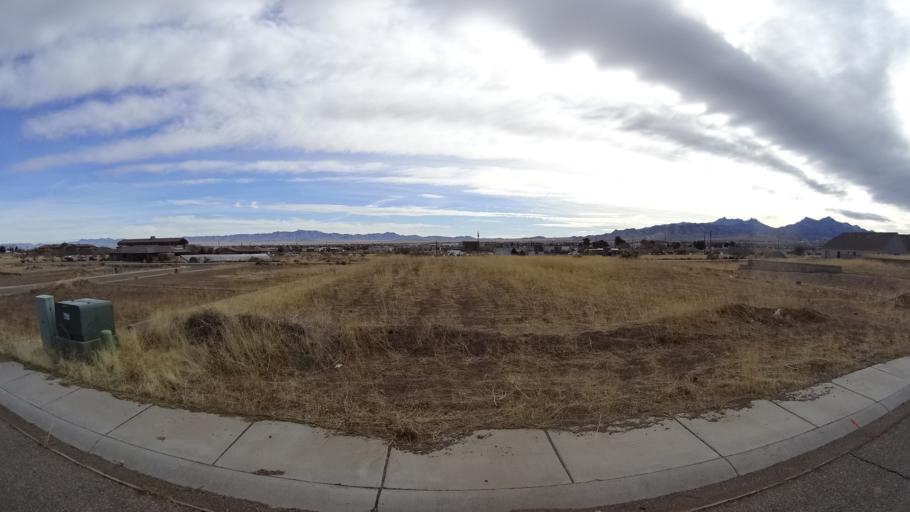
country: US
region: Arizona
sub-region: Mohave County
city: Kingman
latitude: 35.2234
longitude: -114.0458
